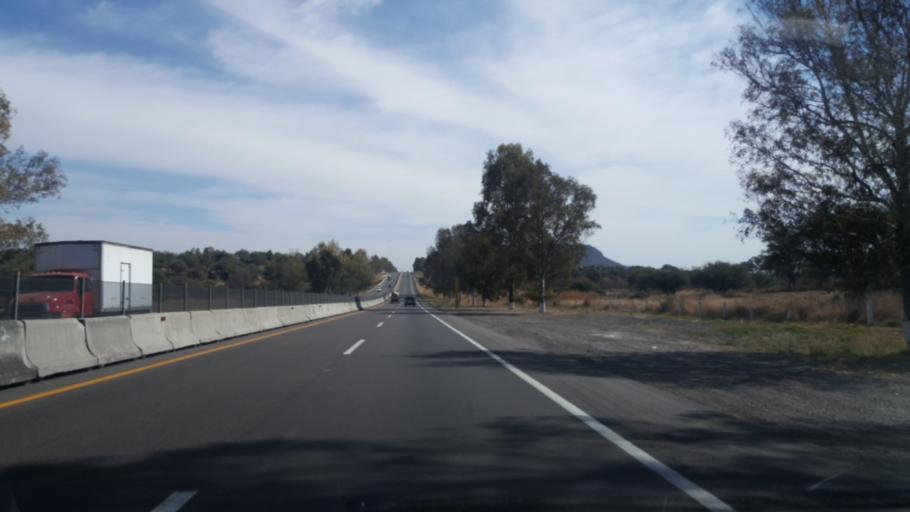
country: MX
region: Jalisco
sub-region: Lagos de Moreno
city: Cristeros [Fraccionamiento]
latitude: 21.3121
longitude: -102.0338
